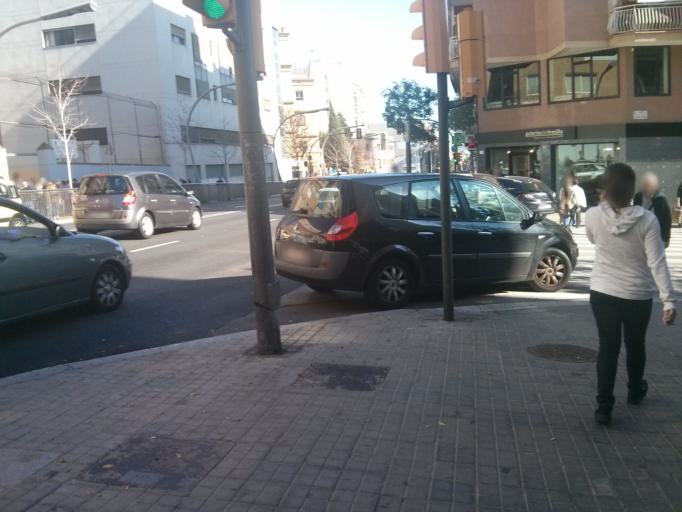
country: ES
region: Catalonia
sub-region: Provincia de Barcelona
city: les Corts
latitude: 41.3759
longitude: 2.1157
